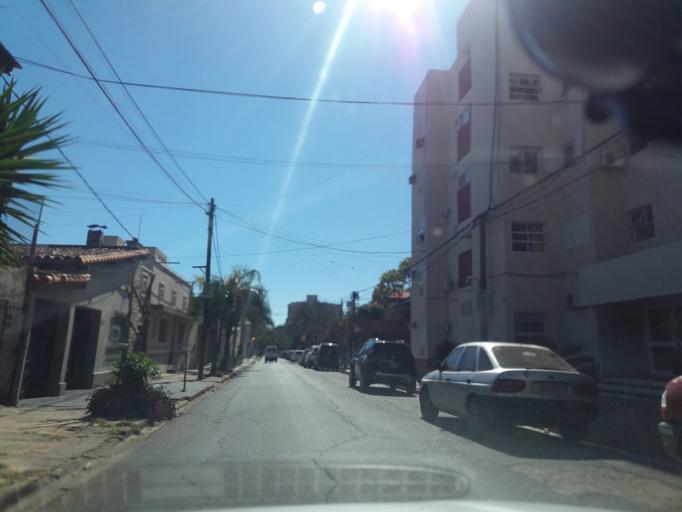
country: AR
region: Corrientes
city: Corrientes
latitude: -27.4726
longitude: -58.8434
